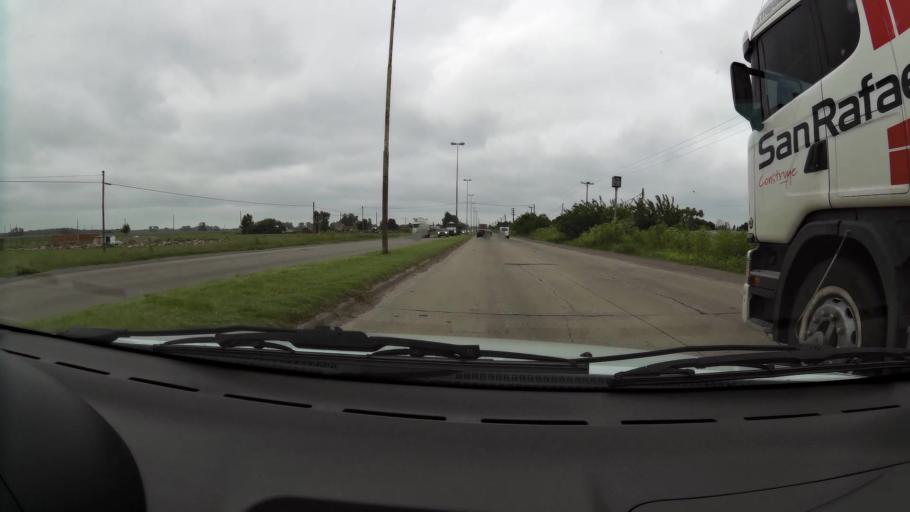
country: AR
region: Buenos Aires
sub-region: Partido de Brandsen
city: Brandsen
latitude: -35.0465
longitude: -58.1043
